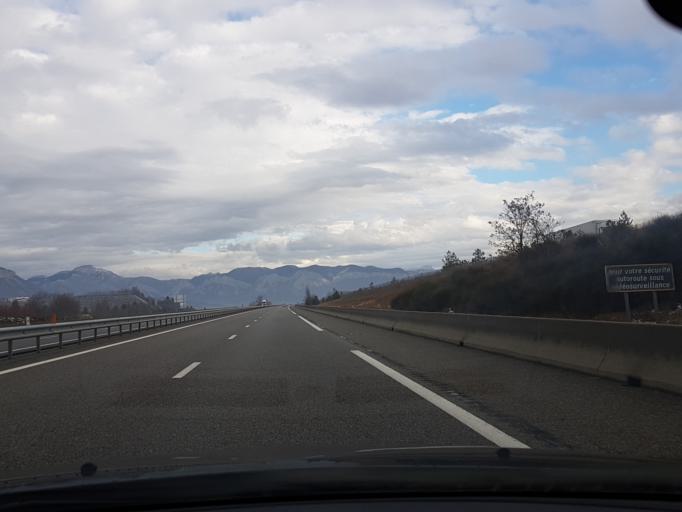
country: FR
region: Provence-Alpes-Cote d'Azur
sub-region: Departement des Hautes-Alpes
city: Laragne-Monteglin
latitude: 44.3005
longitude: 5.9000
